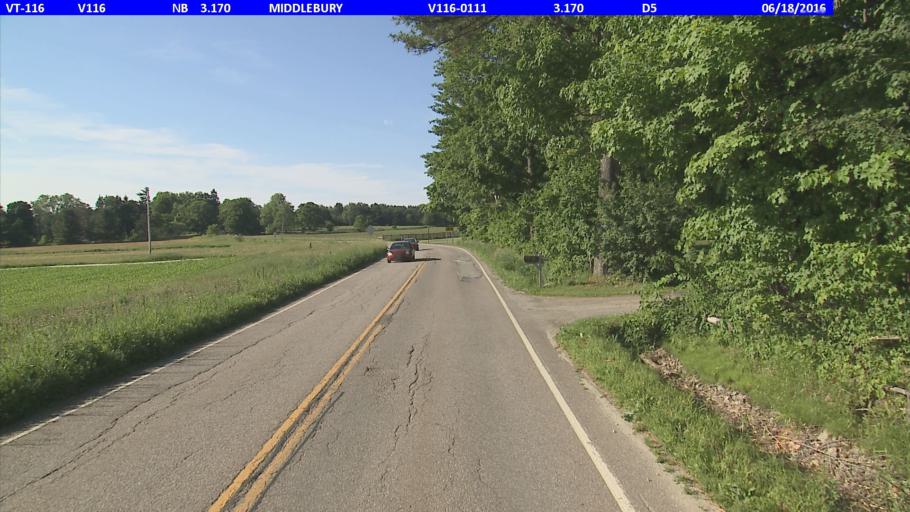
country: US
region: Vermont
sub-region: Addison County
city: Middlebury (village)
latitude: 44.0090
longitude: -73.0973
